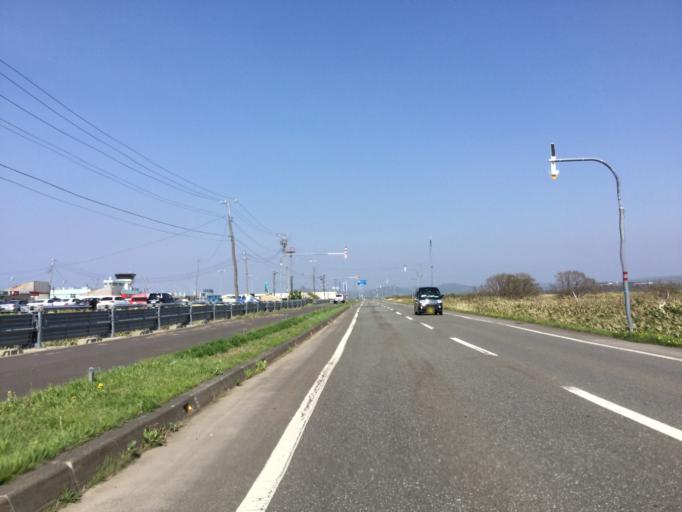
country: JP
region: Hokkaido
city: Makubetsu
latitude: 45.3972
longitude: 141.7941
